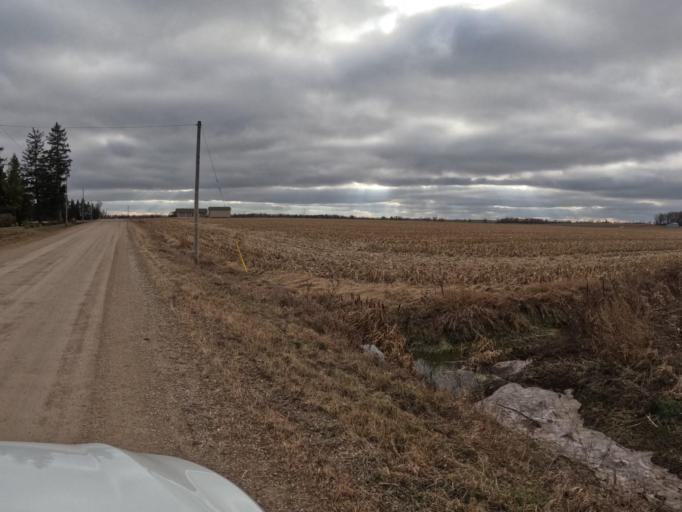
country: CA
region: Ontario
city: Shelburne
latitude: 43.8657
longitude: -80.4009
